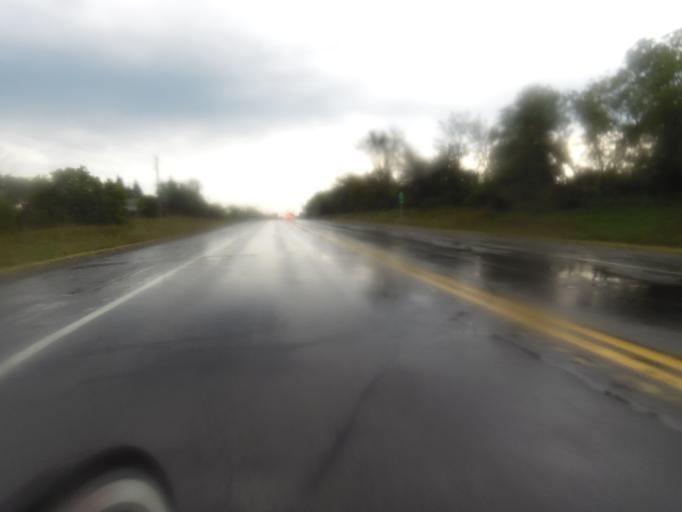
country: CA
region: Ontario
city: Bells Corners
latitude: 45.2199
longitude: -75.7166
